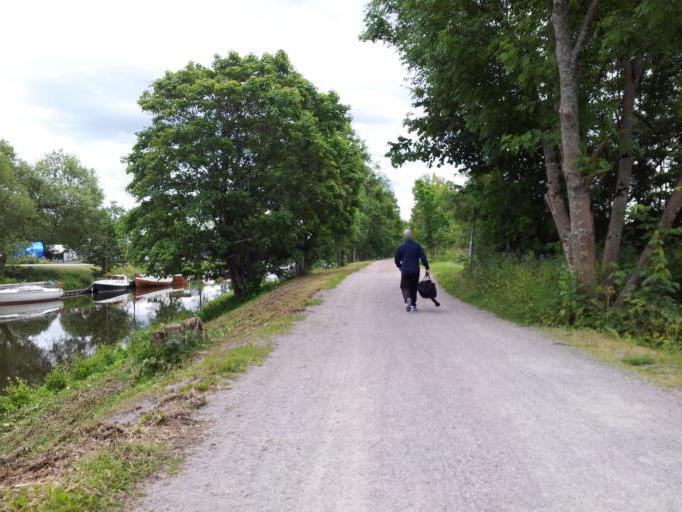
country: SE
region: Uppsala
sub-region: Uppsala Kommun
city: Uppsala
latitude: 59.8451
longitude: 17.6516
